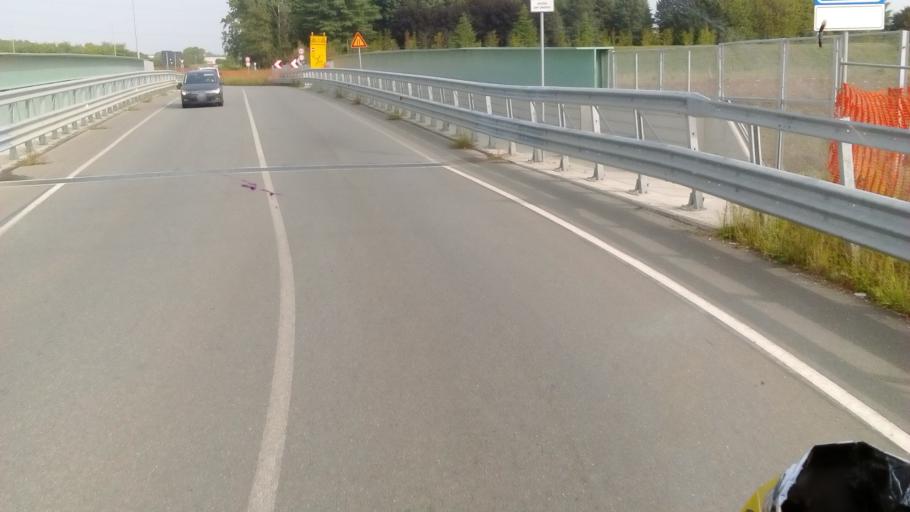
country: IT
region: Lombardy
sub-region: Provincia di Como
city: Rovellasca
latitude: 45.6783
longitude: 9.0549
